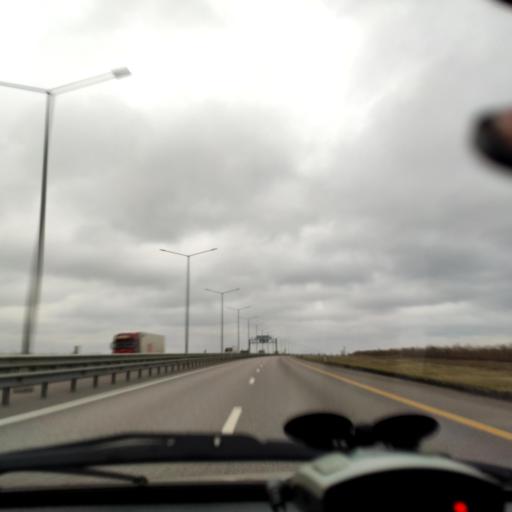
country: RU
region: Voronezj
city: Novaya Usman'
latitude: 51.6018
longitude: 39.3422
